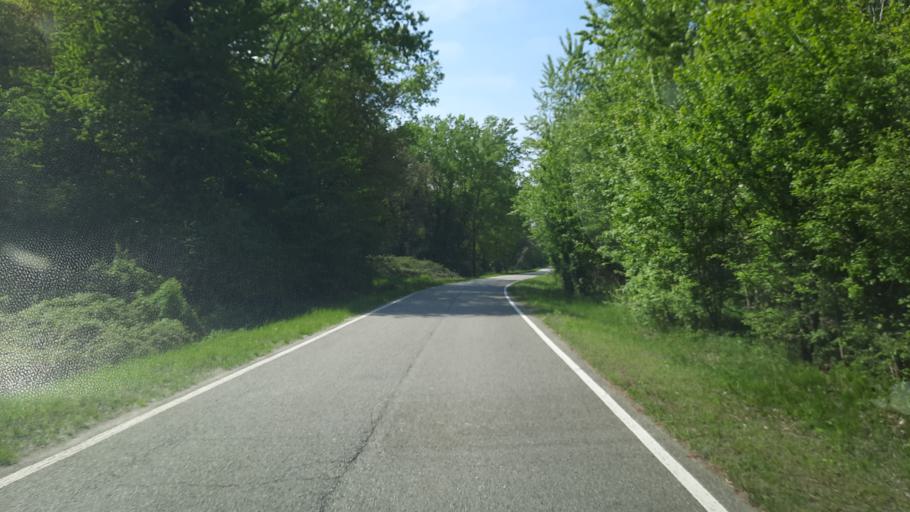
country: IT
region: Piedmont
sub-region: Provincia di Alessandria
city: Camino
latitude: 45.1751
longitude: 8.2784
